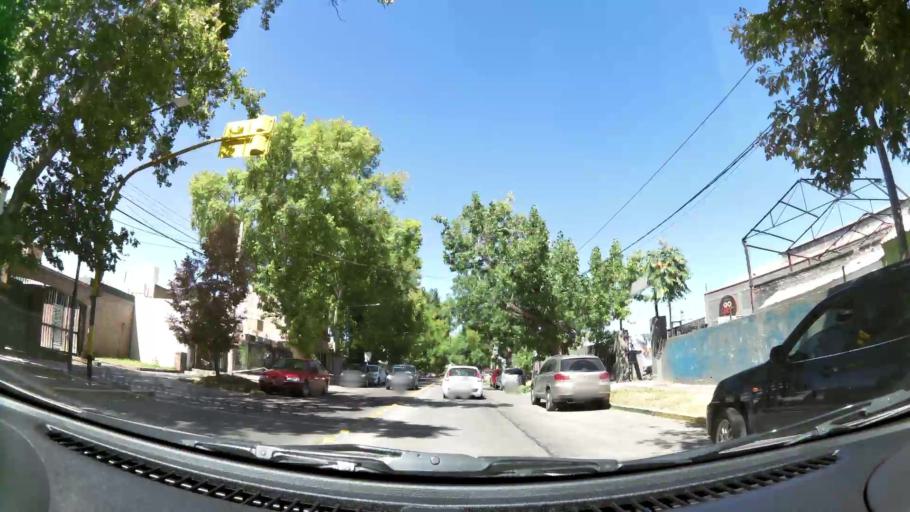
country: AR
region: Mendoza
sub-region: Departamento de Godoy Cruz
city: Godoy Cruz
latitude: -32.9526
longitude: -68.8510
